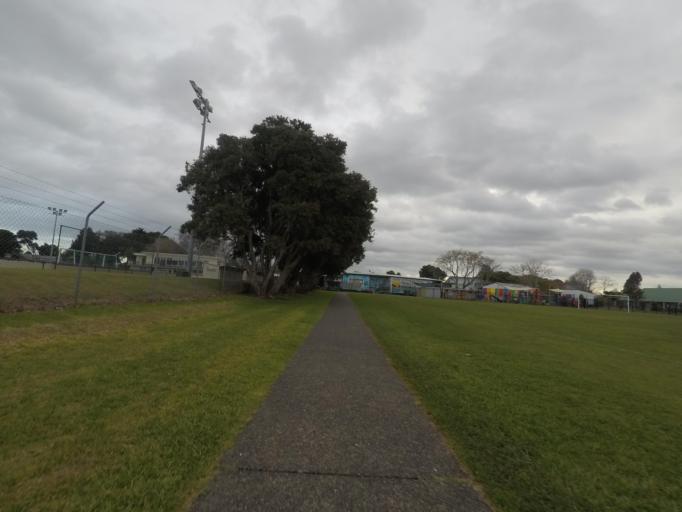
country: NZ
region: Auckland
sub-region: Auckland
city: Rosebank
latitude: -36.8886
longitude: 174.6880
